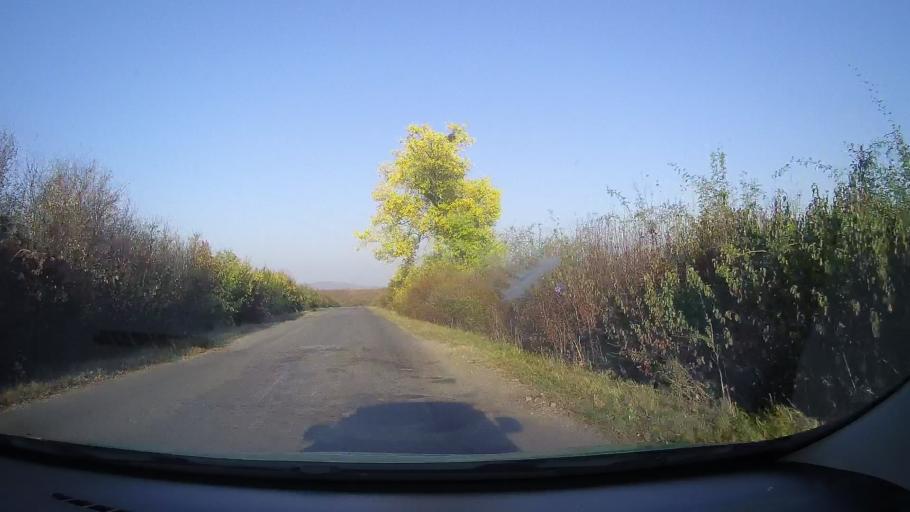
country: RO
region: Arad
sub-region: Comuna Pancota
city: Maderat
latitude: 46.3104
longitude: 21.7432
